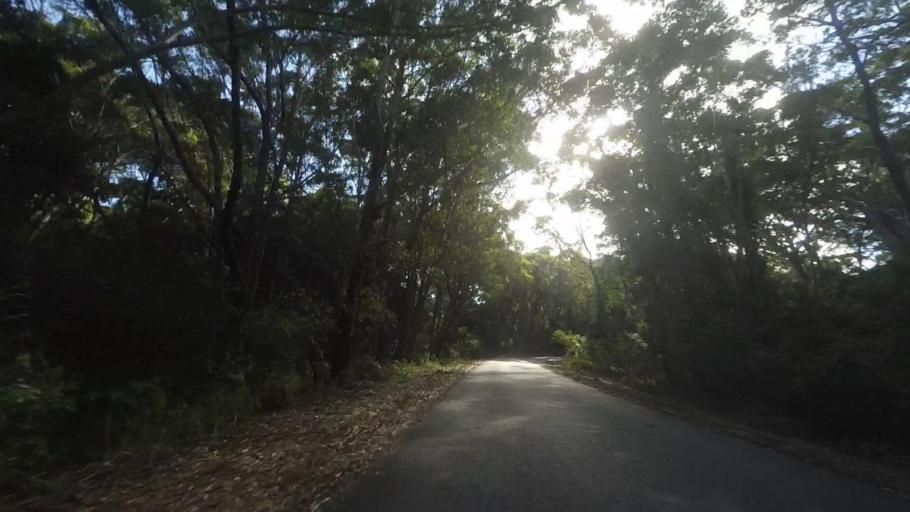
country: AU
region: New South Wales
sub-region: Great Lakes
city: Forster
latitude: -32.4324
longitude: 152.5194
